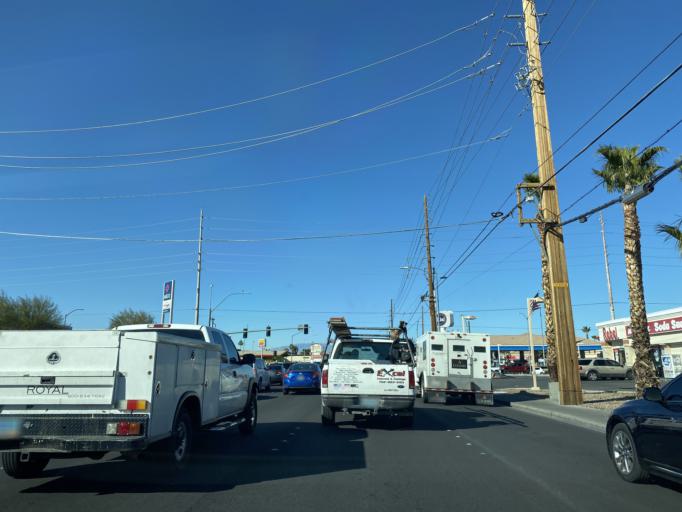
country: US
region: Nevada
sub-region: Clark County
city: Las Vegas
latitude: 36.1435
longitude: -115.1908
